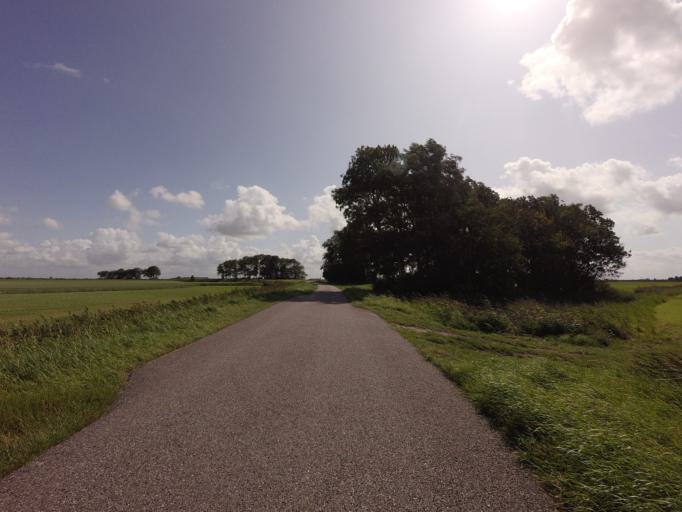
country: NL
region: Friesland
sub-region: Sudwest Fryslan
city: Makkum
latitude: 53.0648
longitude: 5.4466
